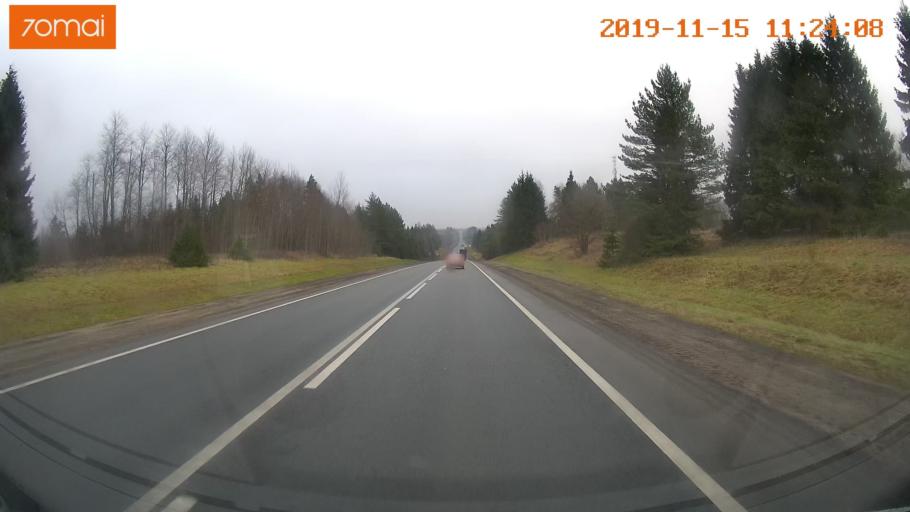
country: RU
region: Vologda
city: Molochnoye
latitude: 59.1555
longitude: 39.3984
